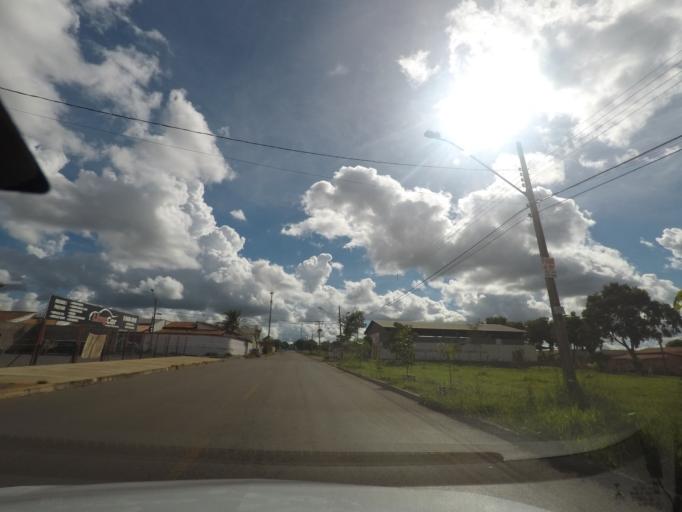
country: BR
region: Goias
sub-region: Goiania
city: Goiania
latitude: -16.7221
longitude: -49.3696
